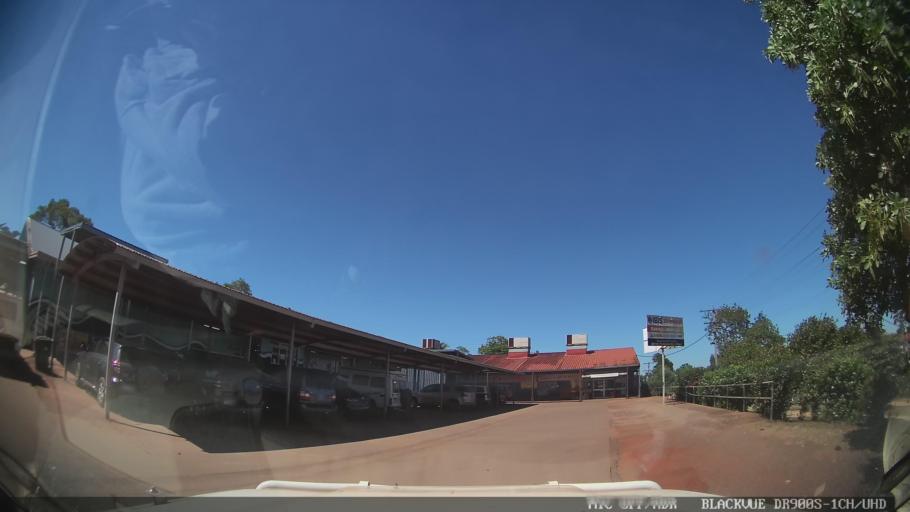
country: AU
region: Queensland
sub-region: Torres
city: Thursday Island
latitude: -10.8882
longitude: 142.3883
